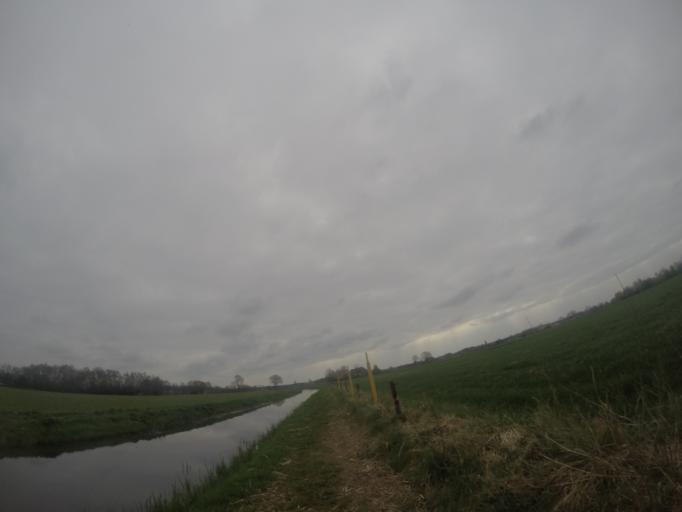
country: NL
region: Gelderland
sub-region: Gemeente Zutphen
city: Leesten
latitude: 52.1136
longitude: 6.2361
